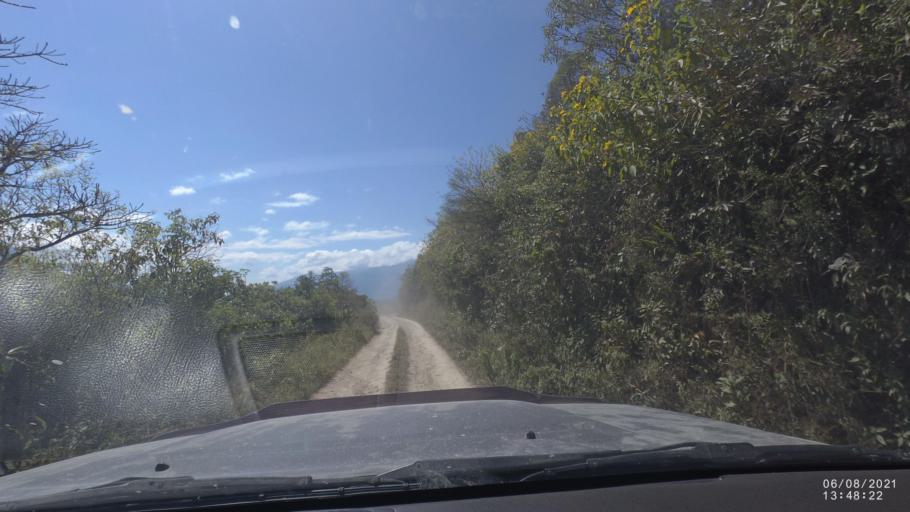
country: BO
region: La Paz
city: Quime
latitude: -16.6640
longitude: -66.7259
